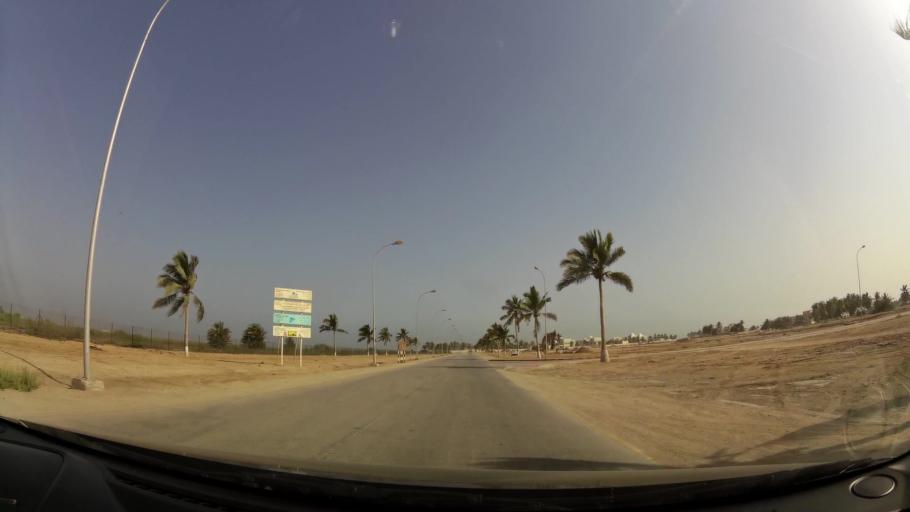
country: OM
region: Zufar
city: Salalah
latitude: 17.0015
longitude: 54.0656
